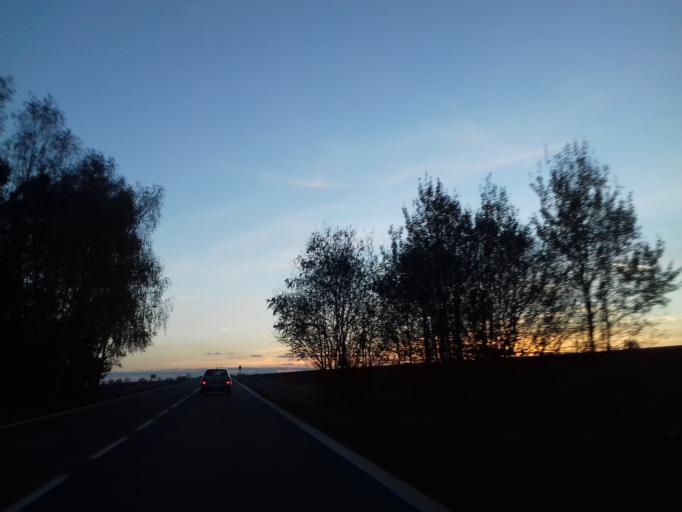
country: CZ
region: Vysocina
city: Chotebor
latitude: 49.6561
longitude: 15.7028
